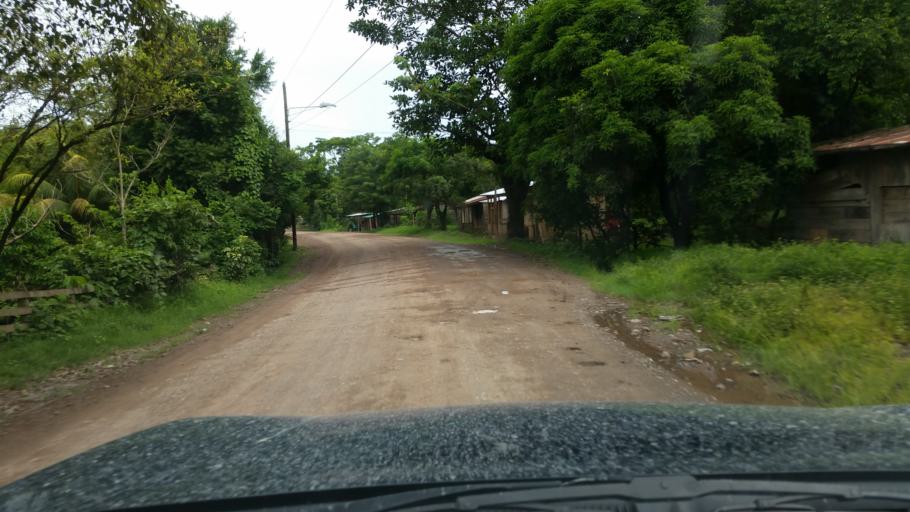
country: NI
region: Atlantico Norte (RAAN)
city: Siuna
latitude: 13.4942
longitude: -84.8446
